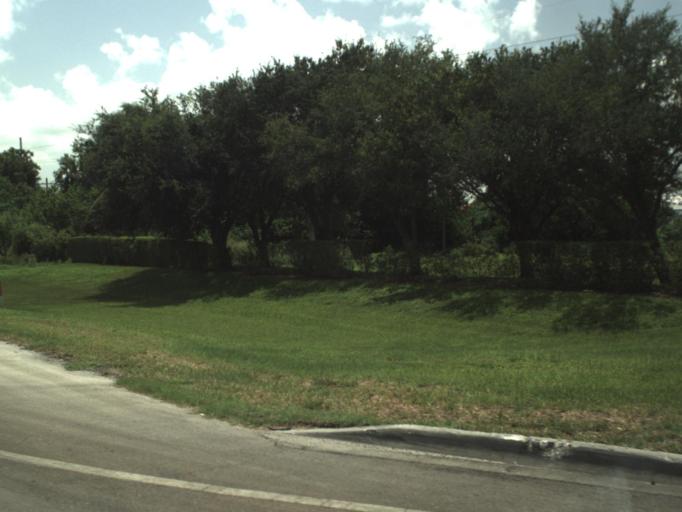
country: US
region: Florida
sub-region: Palm Beach County
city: Belle Glade
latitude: 26.7065
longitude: -80.6681
